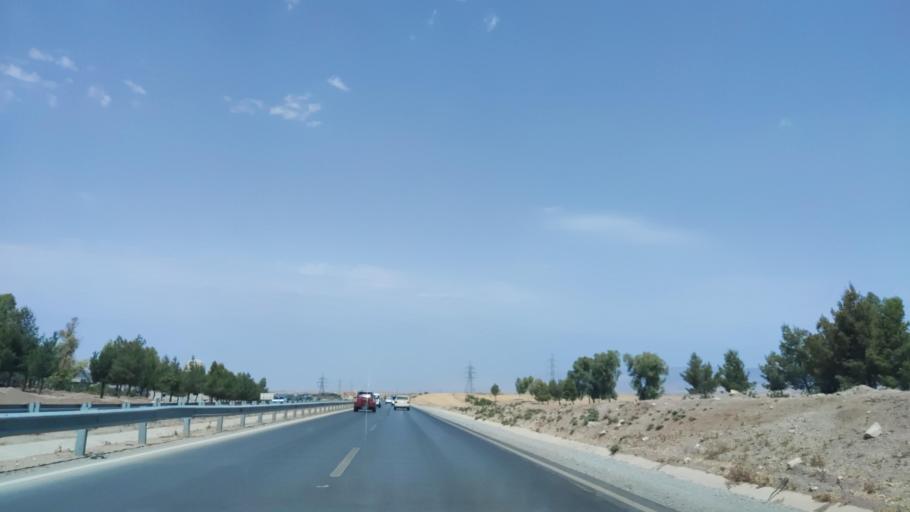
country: IQ
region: Arbil
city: Shaqlawah
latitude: 36.5016
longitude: 44.3572
